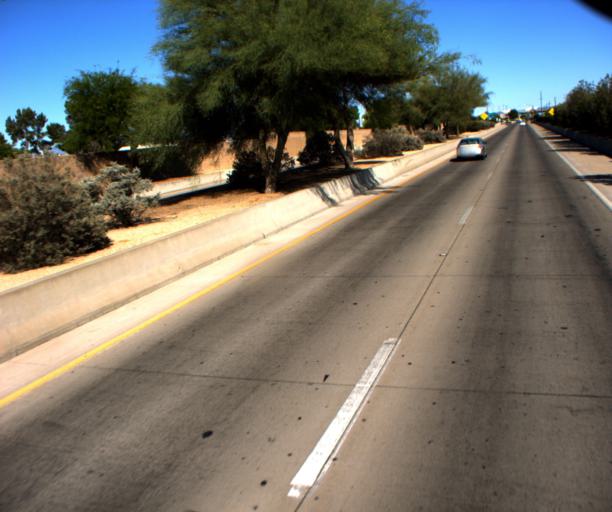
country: US
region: Arizona
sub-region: Pima County
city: Tucson
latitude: 32.1954
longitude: -110.9232
